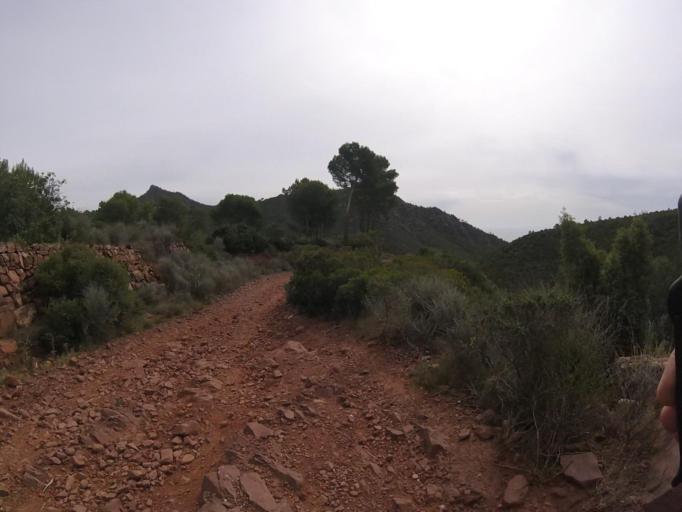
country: ES
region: Valencia
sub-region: Provincia de Castello
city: Benicassim
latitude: 40.0707
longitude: 0.0351
